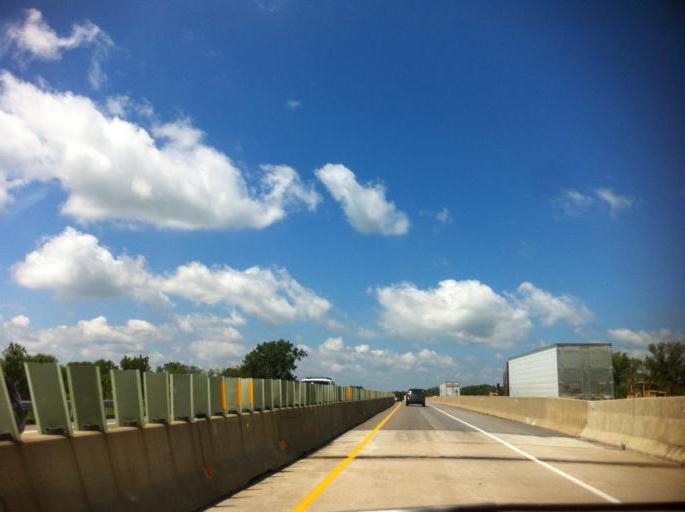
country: US
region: Ohio
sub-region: Sandusky County
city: Mount Carmel
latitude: 41.3571
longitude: -82.8923
